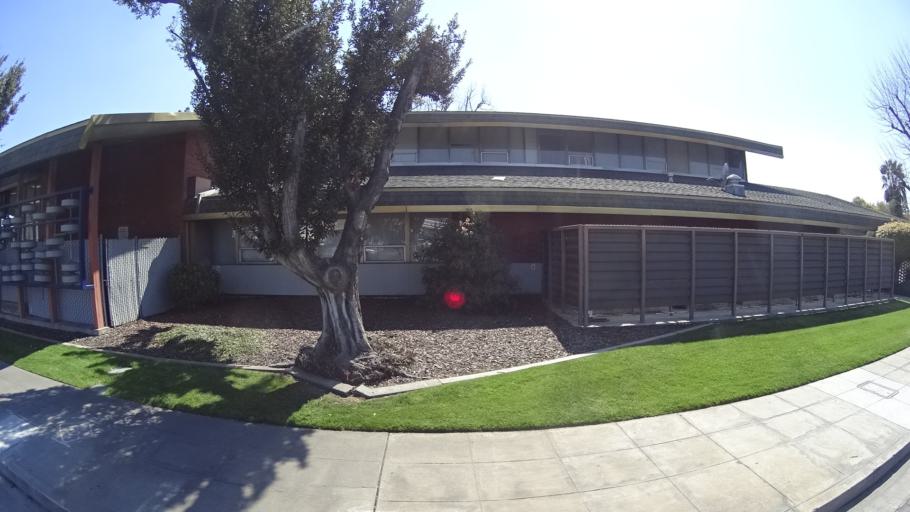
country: US
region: California
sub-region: Fresno County
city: Fresno
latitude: 36.7940
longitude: -119.7915
